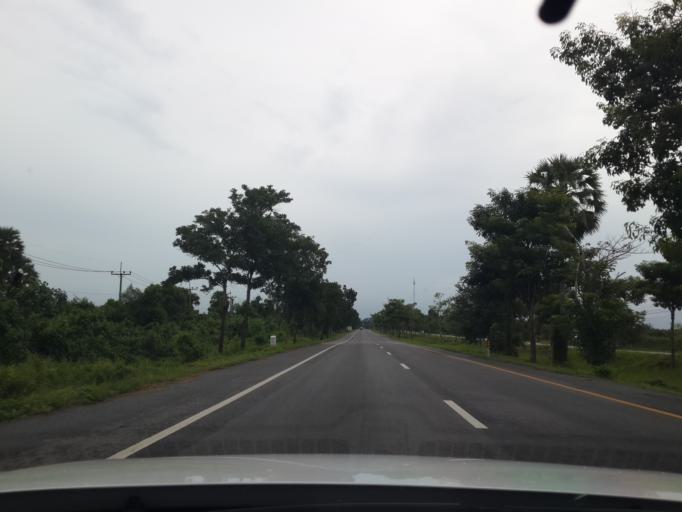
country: TH
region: Pattani
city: Khok Pho
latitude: 6.8216
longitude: 101.0633
